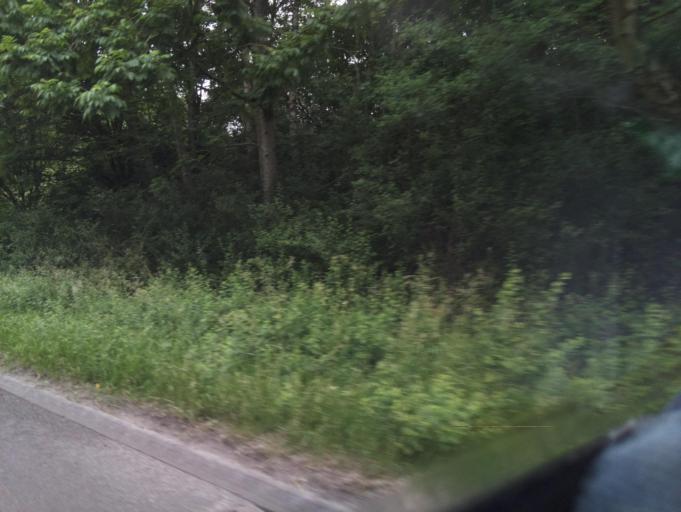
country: GB
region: England
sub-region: Staffordshire
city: Burton upon Trent
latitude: 52.8551
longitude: -1.6797
